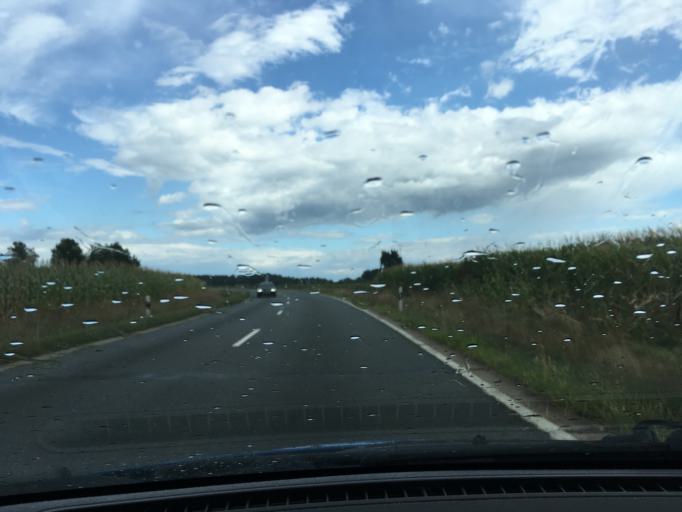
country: DE
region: Lower Saxony
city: Wietzendorf
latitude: 52.9614
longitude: 9.9700
